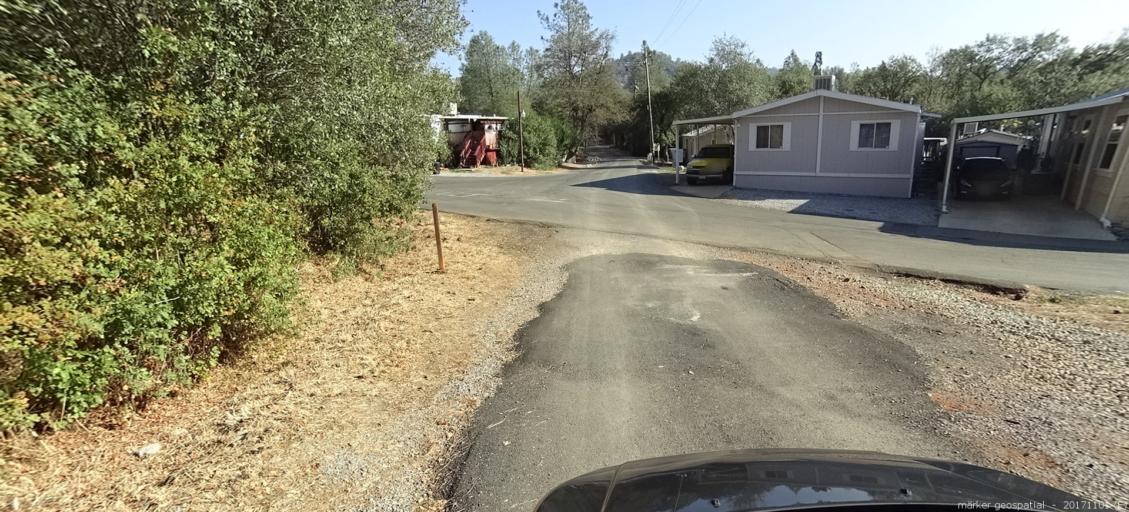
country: US
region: California
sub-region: Shasta County
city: Shasta Lake
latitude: 40.7124
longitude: -122.3375
